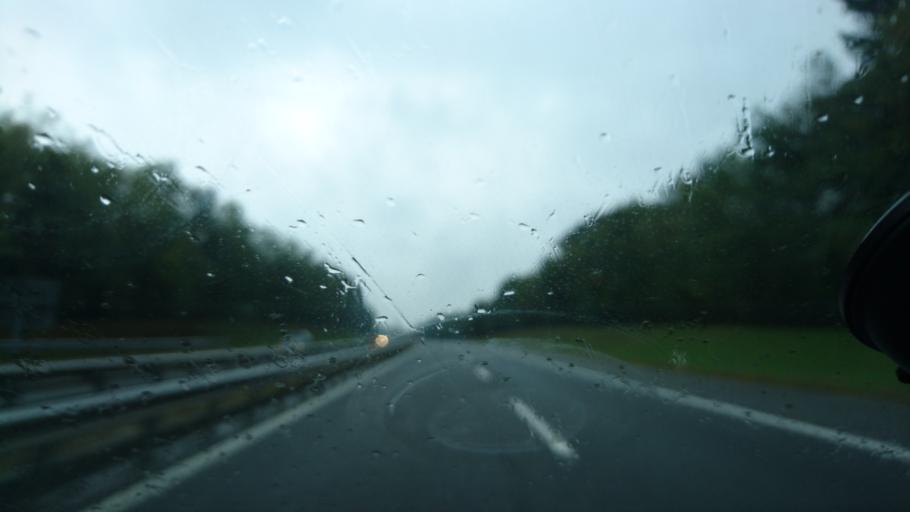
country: IT
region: Piedmont
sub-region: Provincia di Novara
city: Bogogno
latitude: 45.6679
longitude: 8.5206
